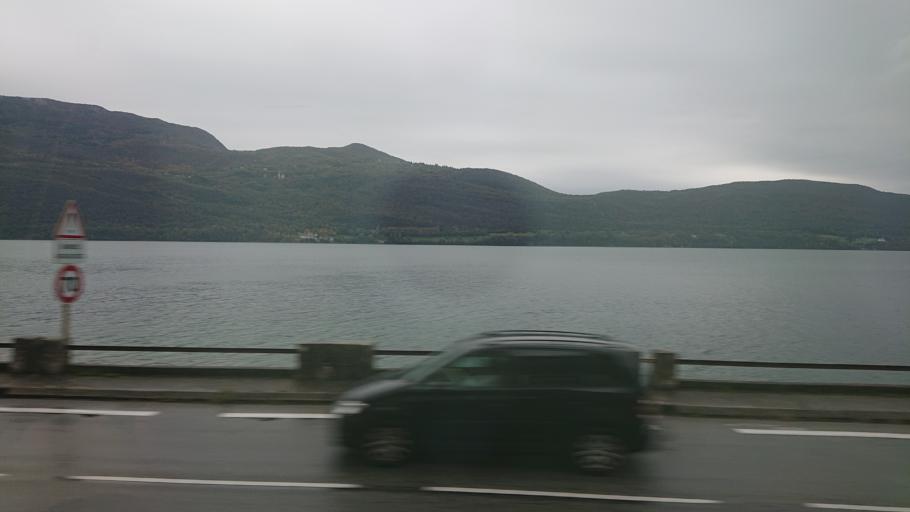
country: FR
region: Rhone-Alpes
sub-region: Departement de la Savoie
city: Brison-Saint-Innocent
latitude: 45.7620
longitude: 5.8705
